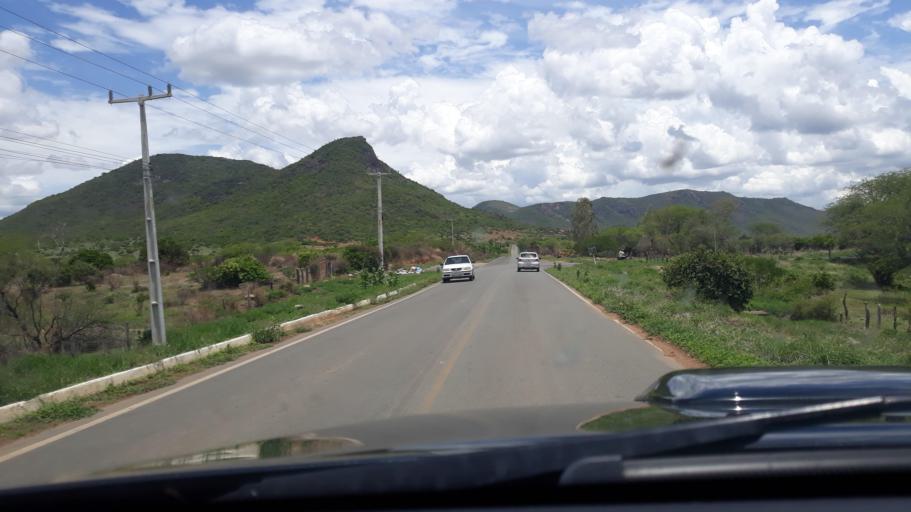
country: BR
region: Bahia
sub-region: Guanambi
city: Guanambi
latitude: -14.2720
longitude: -42.7106
